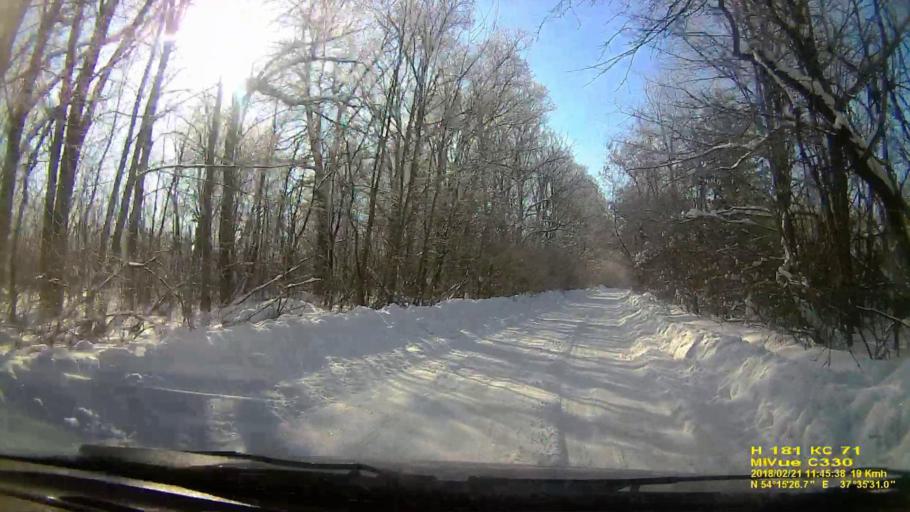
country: RU
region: Tula
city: Gorelki
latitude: 54.2574
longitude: 37.5919
